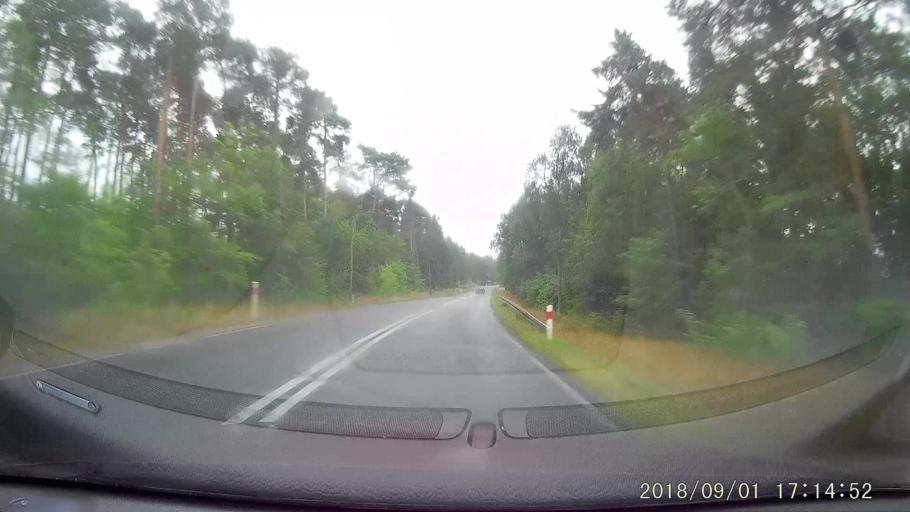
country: PL
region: Lubusz
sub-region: Powiat zielonogorski
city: Nowogrod Bobrzanski
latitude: 51.7803
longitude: 15.2617
